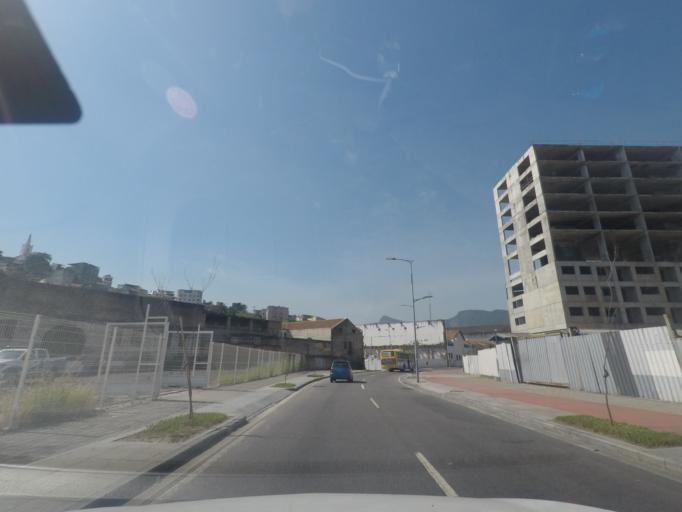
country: BR
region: Rio de Janeiro
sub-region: Rio De Janeiro
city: Rio de Janeiro
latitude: -22.9027
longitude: -43.2064
